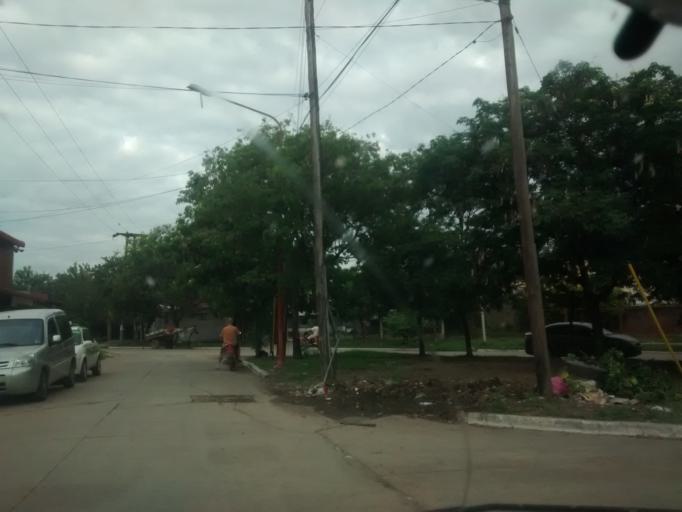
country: AR
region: Chaco
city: Fontana
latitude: -27.4445
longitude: -59.0154
